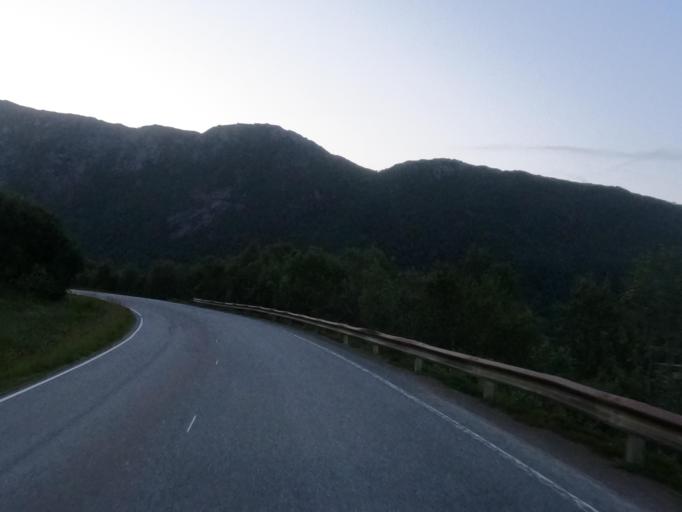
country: NO
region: Nordland
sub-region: Lodingen
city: Lodingen
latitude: 68.5532
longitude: 15.7520
